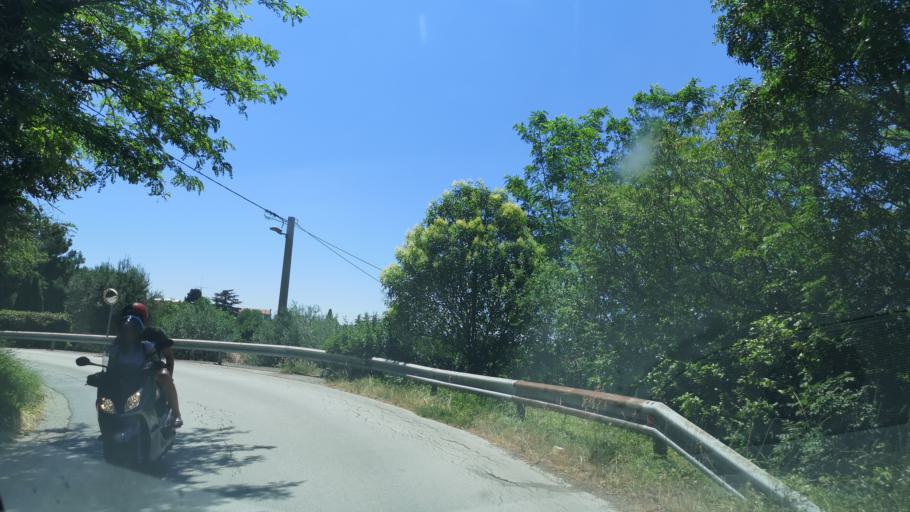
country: SI
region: Piran-Pirano
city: Portoroz
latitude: 45.5214
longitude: 13.5854
